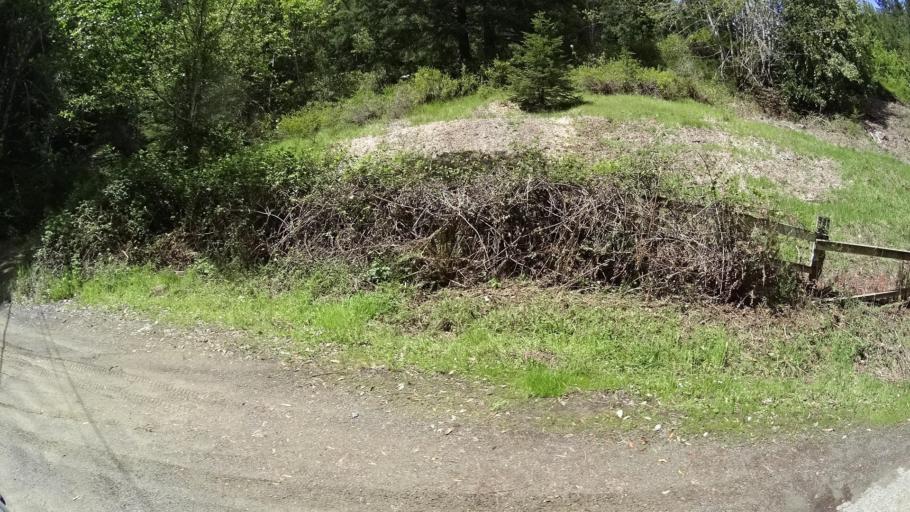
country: US
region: California
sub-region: Humboldt County
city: Blue Lake
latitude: 40.7660
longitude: -123.9478
